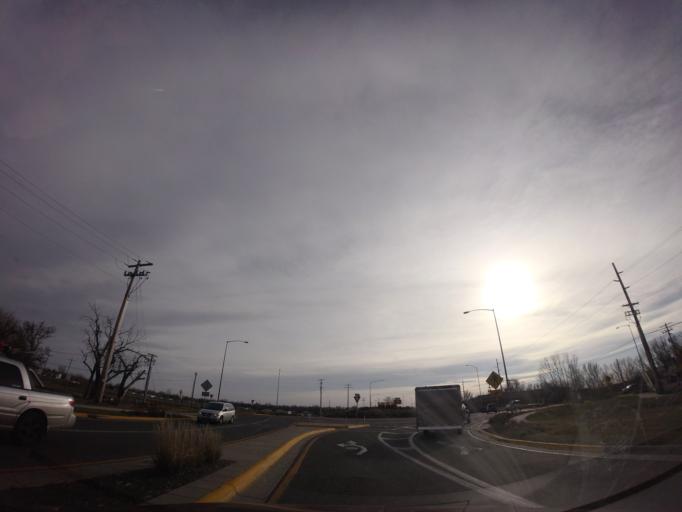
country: US
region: Montana
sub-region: Yellowstone County
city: Billings
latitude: 45.7700
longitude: -108.6176
